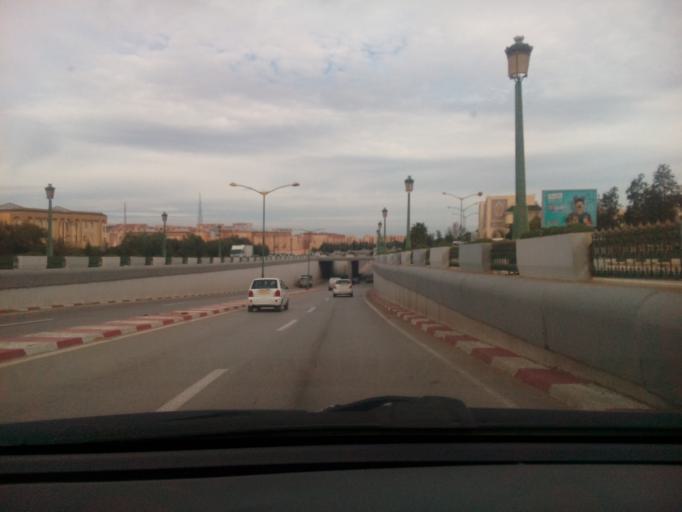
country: DZ
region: Tlemcen
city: Mansoura
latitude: 34.8924
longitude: -1.3557
